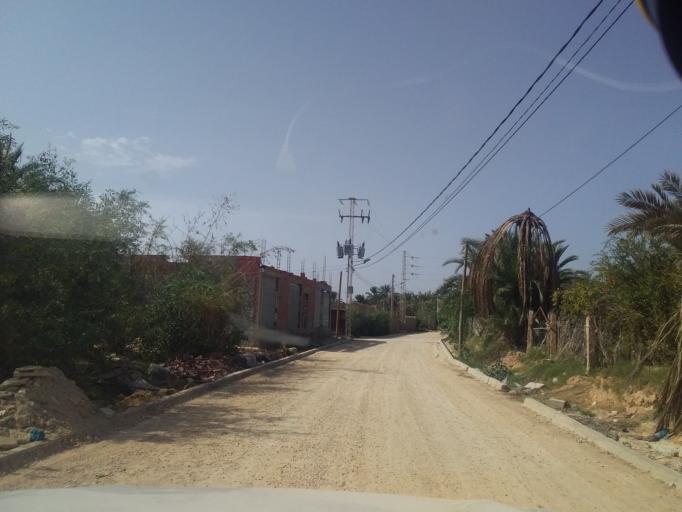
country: TN
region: Qabis
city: Gabes
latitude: 33.6243
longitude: 10.2848
